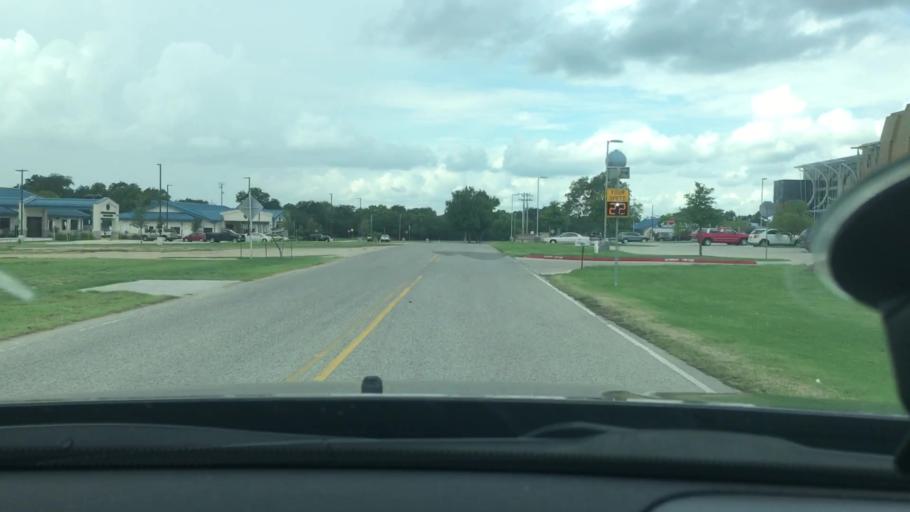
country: US
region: Oklahoma
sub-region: Johnston County
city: Tishomingo
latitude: 34.2336
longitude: -96.6628
